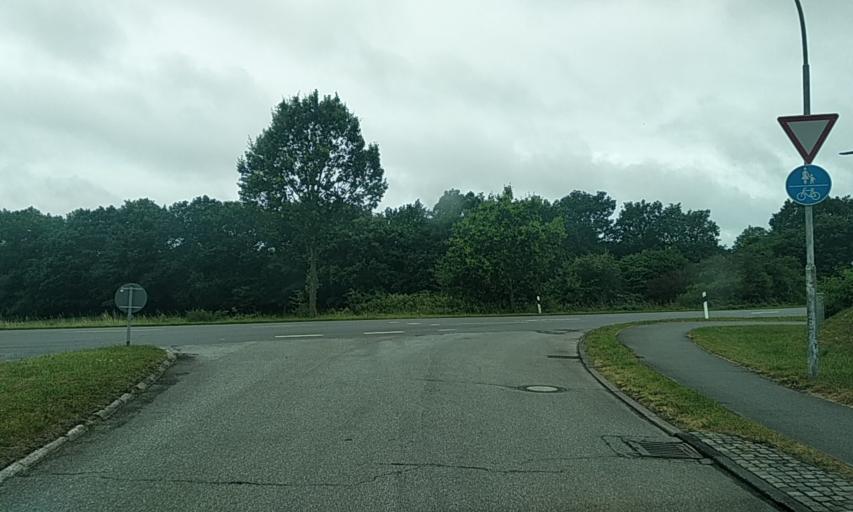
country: DE
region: Schleswig-Holstein
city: Schleswig
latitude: 54.5306
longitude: 9.5829
